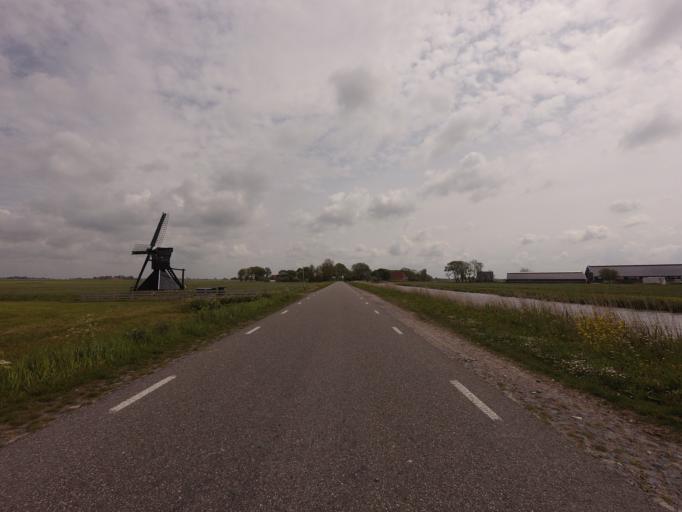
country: NL
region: Friesland
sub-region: Sudwest Fryslan
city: Bolsward
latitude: 53.1000
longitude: 5.5182
